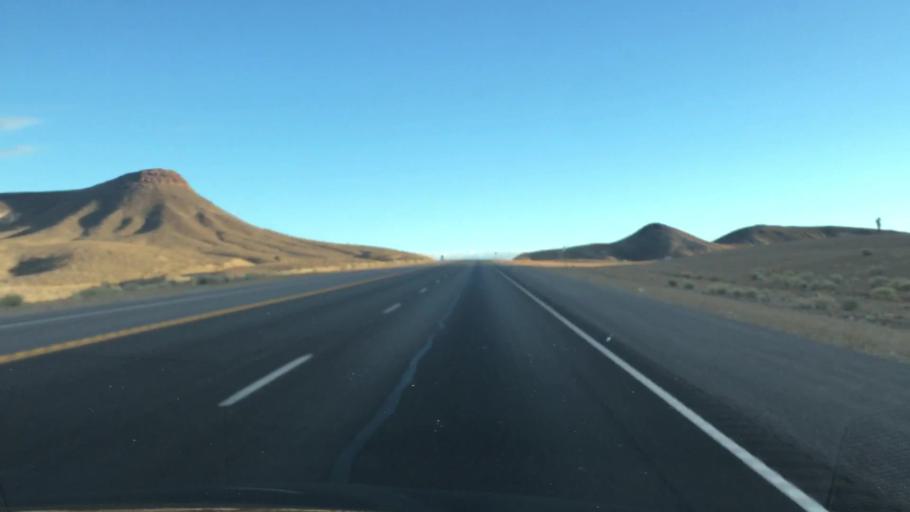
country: US
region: Nevada
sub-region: Esmeralda County
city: Goldfield
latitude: 37.6866
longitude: -117.2323
